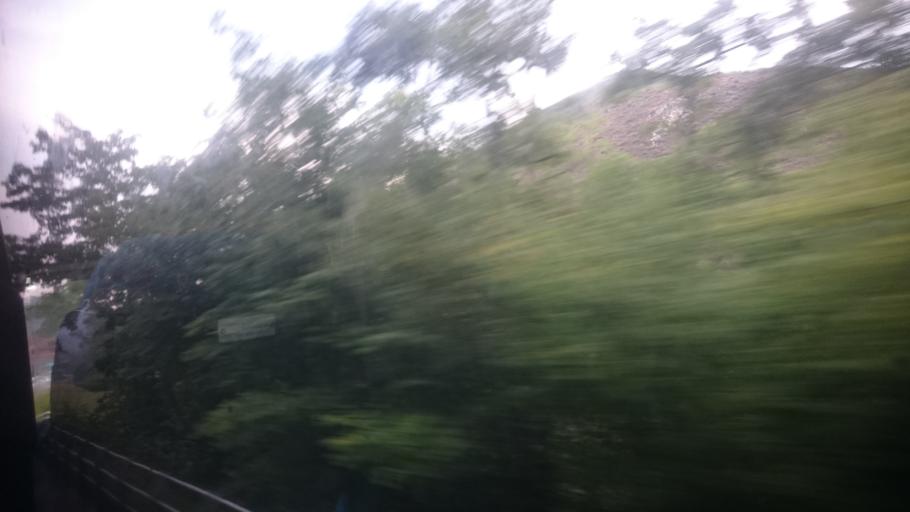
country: ES
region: Asturias
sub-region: Province of Asturias
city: Cangas de Onis
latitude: 43.3327
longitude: -5.0831
